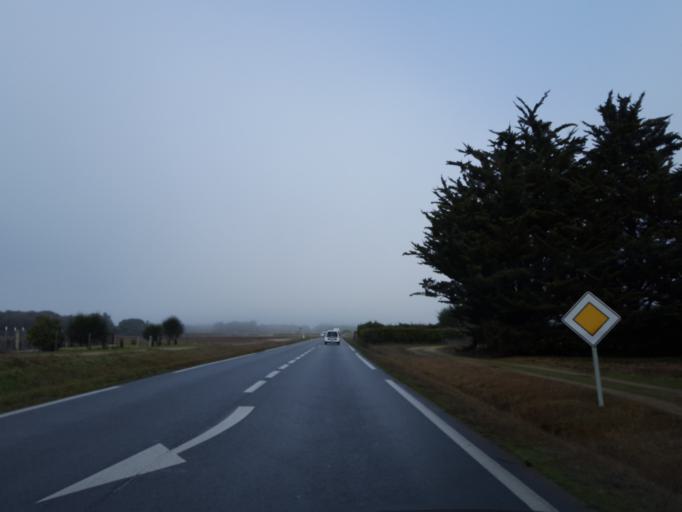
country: FR
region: Poitou-Charentes
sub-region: Departement de la Charente-Maritime
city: La Flotte
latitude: 46.1804
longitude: -1.3345
